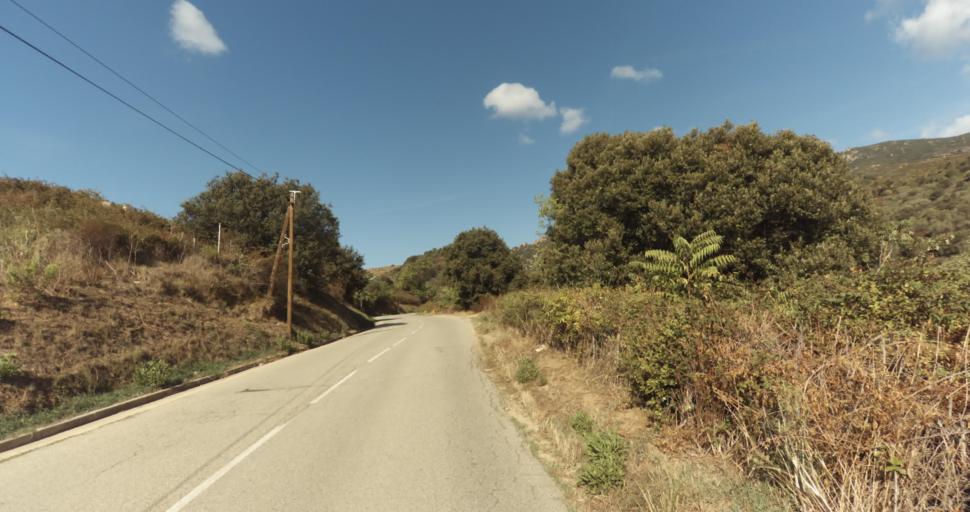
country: FR
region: Corsica
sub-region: Departement de la Corse-du-Sud
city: Ajaccio
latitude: 41.9295
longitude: 8.6977
